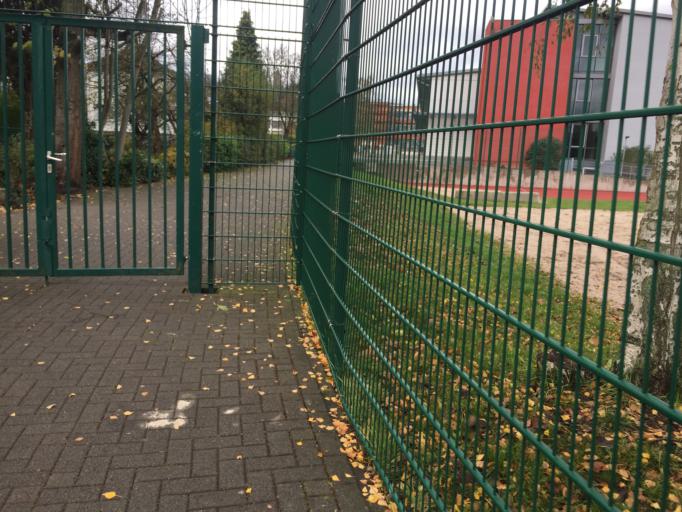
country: DE
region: Hesse
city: Dillenburg
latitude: 50.7318
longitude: 8.2904
